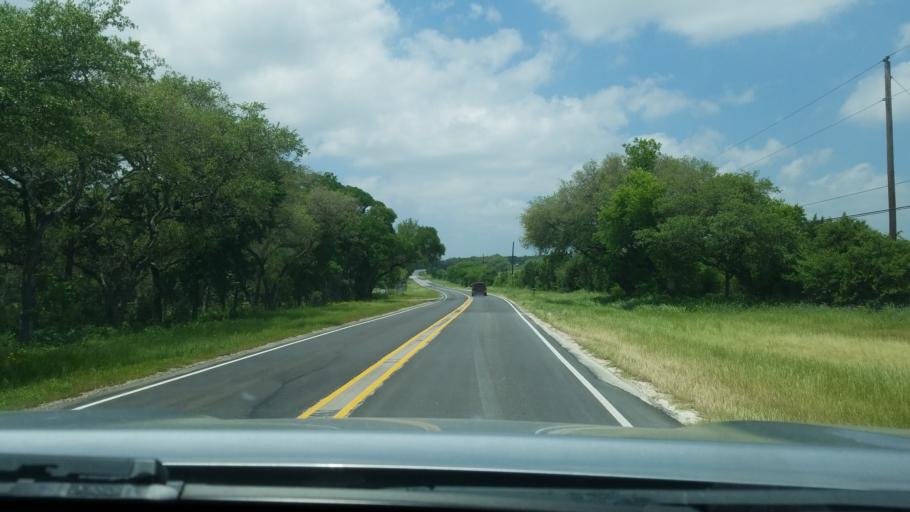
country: US
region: Texas
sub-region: Hays County
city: Dripping Springs
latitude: 30.1503
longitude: -98.0611
